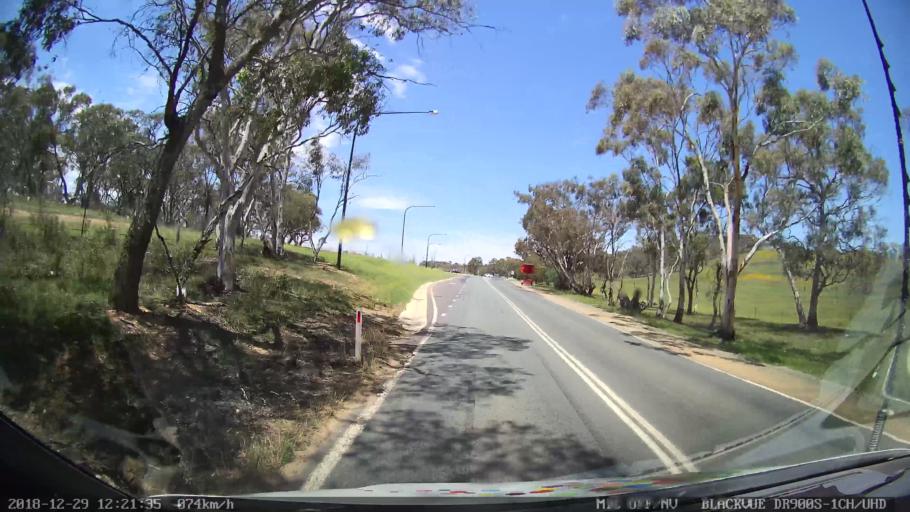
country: AU
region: New South Wales
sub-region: Queanbeyan
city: Queanbeyan
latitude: -35.4152
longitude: 149.2230
